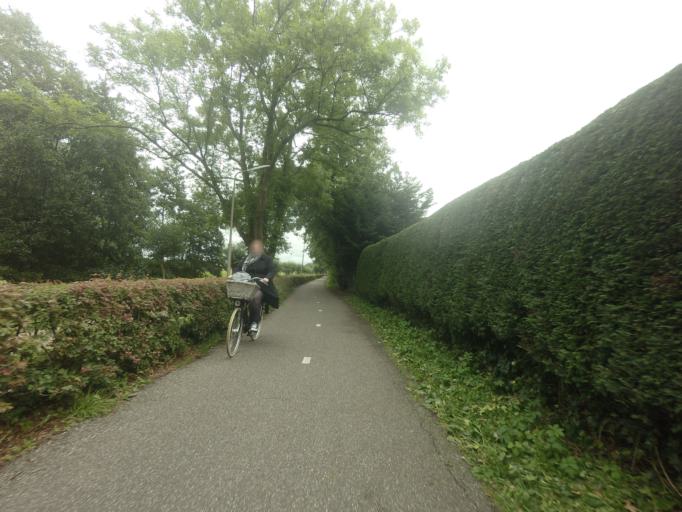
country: NL
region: North Holland
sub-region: Gemeente Bloemendaal
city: Bloemendaal
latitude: 52.4169
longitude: 4.6327
